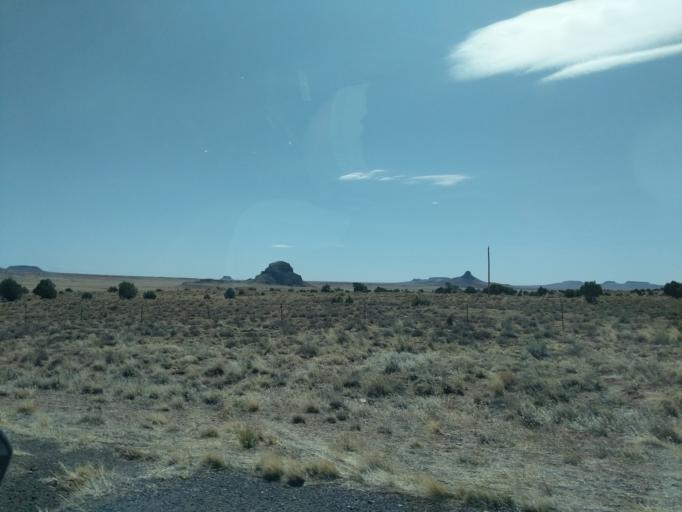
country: US
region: Arizona
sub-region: Navajo County
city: Dilkon
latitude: 35.3930
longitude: -110.0845
